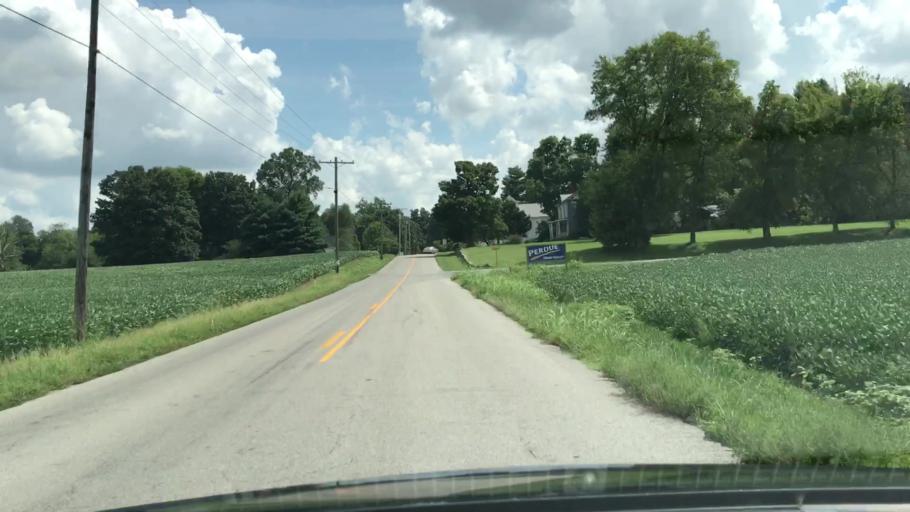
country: US
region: Kentucky
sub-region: Todd County
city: Guthrie
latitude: 36.7182
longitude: -87.0730
